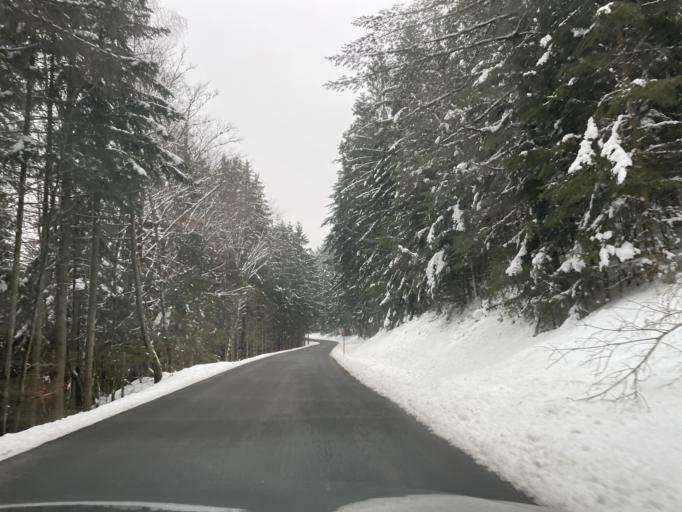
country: DE
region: Bavaria
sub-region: Lower Bavaria
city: Viechtach
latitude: 49.1353
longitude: 12.9160
